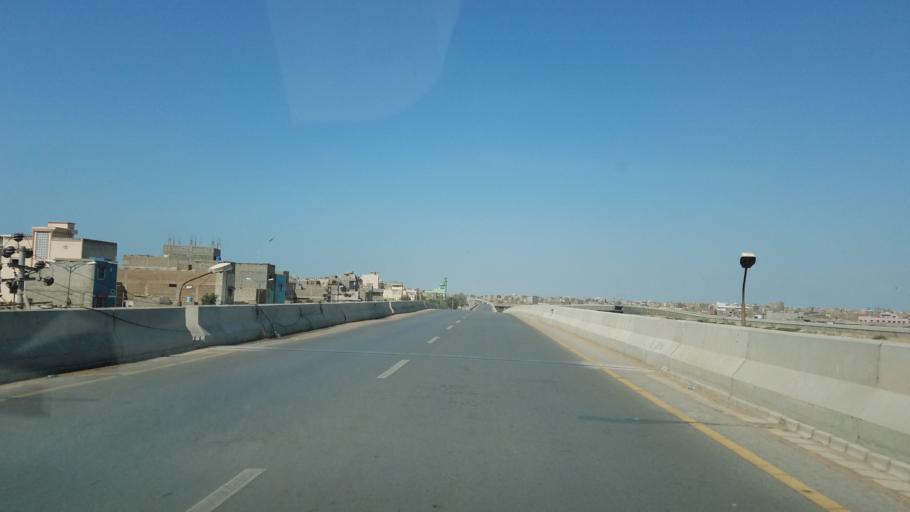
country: PK
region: Sindh
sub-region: Karachi District
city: Karachi
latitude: 24.8807
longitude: 67.0039
